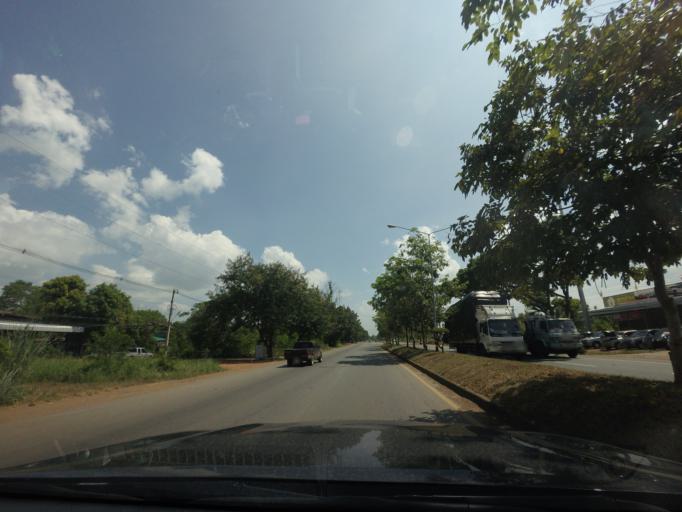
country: TH
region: Phetchabun
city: Nong Phai
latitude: 16.0591
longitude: 101.0744
